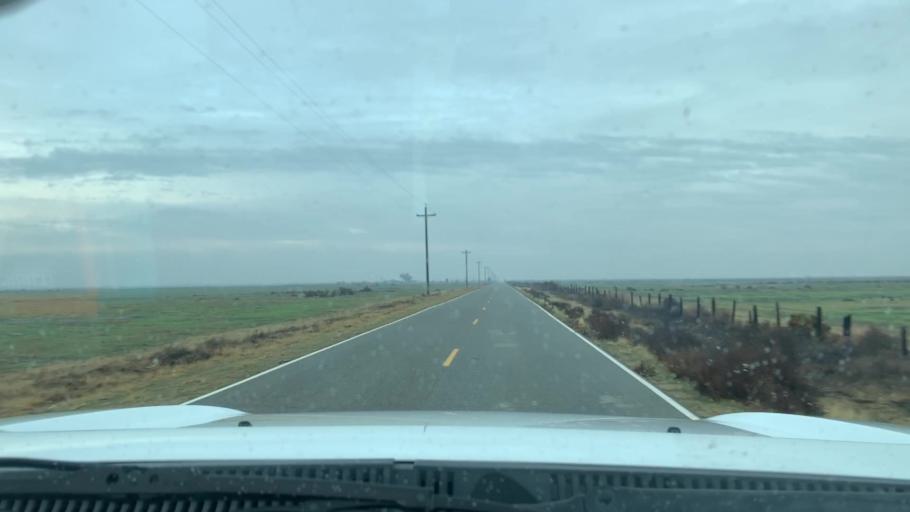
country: US
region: California
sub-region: Kern County
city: Lost Hills
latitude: 35.6905
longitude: -119.5797
